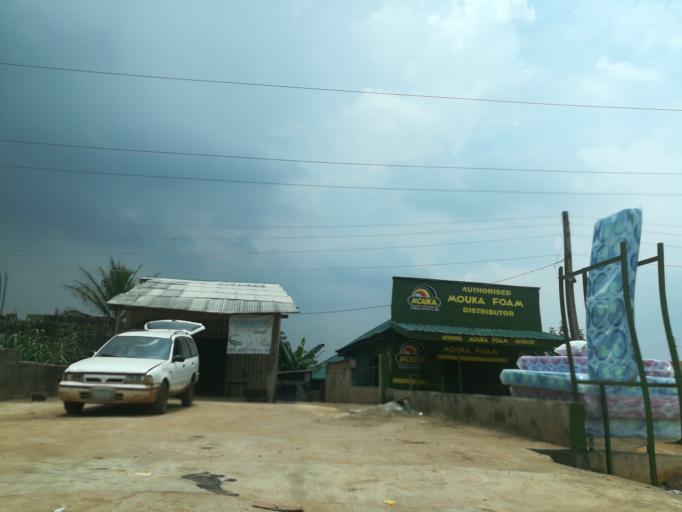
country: NG
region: Lagos
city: Ikorodu
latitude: 6.6068
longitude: 3.5856
